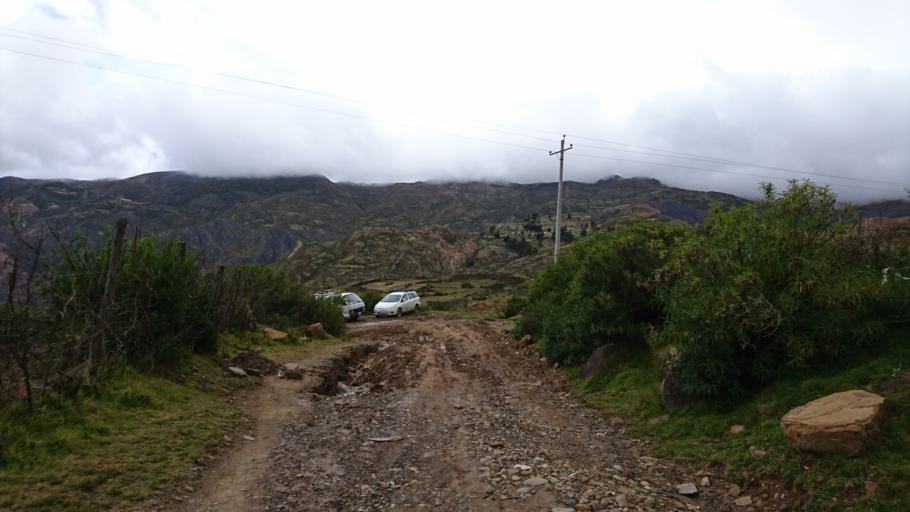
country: BO
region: La Paz
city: La Paz
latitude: -16.5471
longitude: -67.9949
